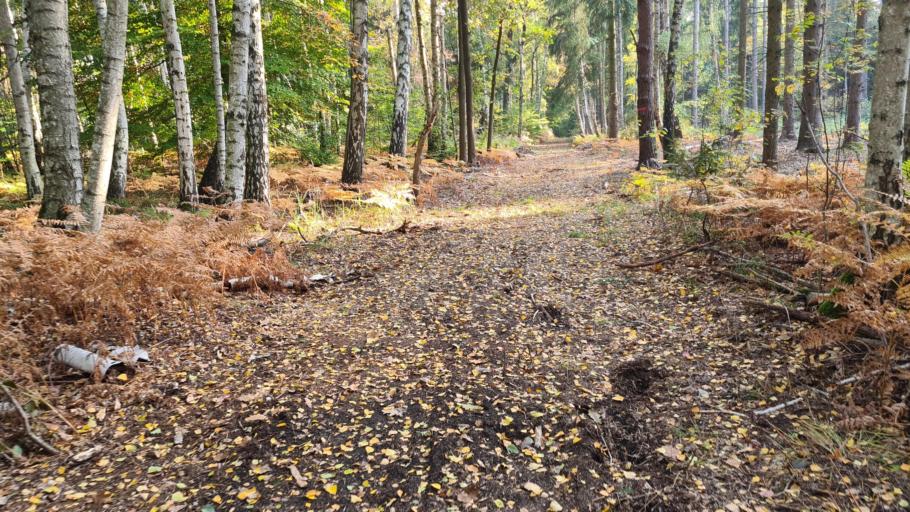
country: DE
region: Brandenburg
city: Doberlug-Kirchhain
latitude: 51.6272
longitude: 13.5216
